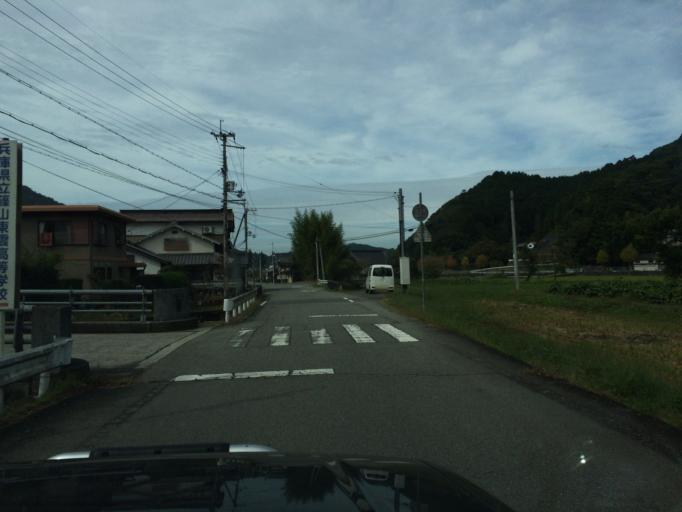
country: JP
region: Hyogo
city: Sasayama
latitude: 35.0717
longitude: 135.3500
